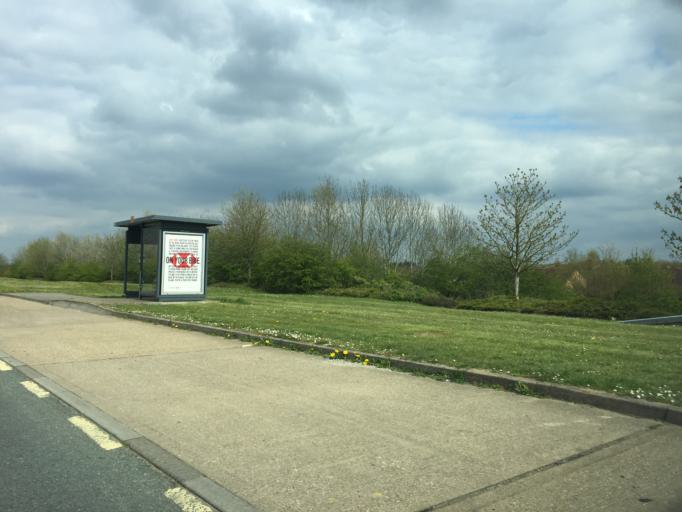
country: GB
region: England
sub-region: Milton Keynes
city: Shenley Church End
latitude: 52.0050
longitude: -0.7886
